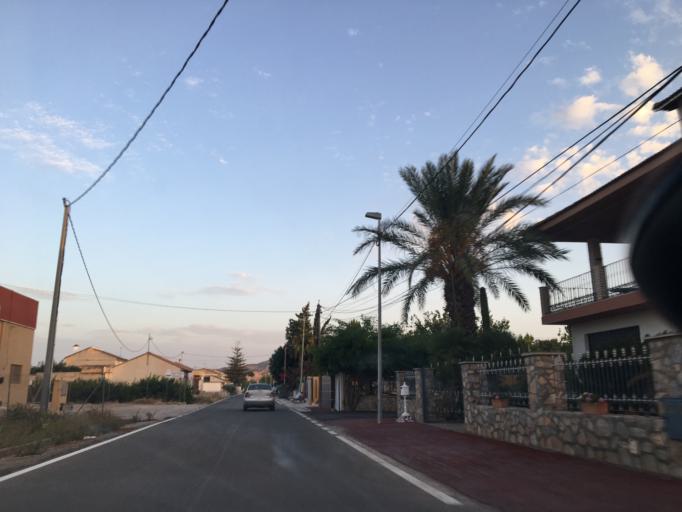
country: ES
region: Murcia
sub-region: Murcia
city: Santomera
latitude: 38.0299
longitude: -1.0591
